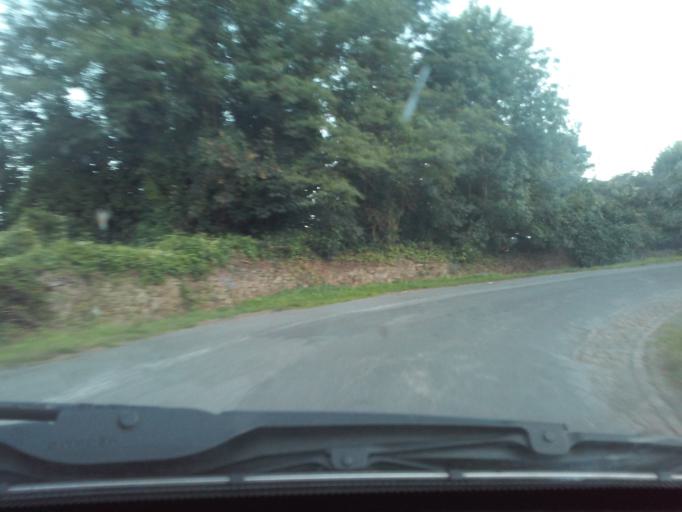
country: FR
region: Brittany
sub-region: Departement des Cotes-d'Armor
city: Dinan
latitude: 48.4526
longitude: -2.0377
